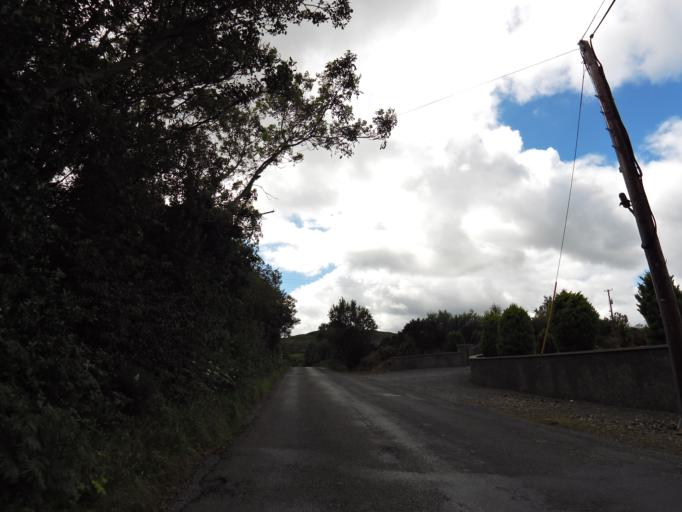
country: IE
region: Connaught
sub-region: County Galway
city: Oughterard
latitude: 53.4179
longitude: -9.3293
